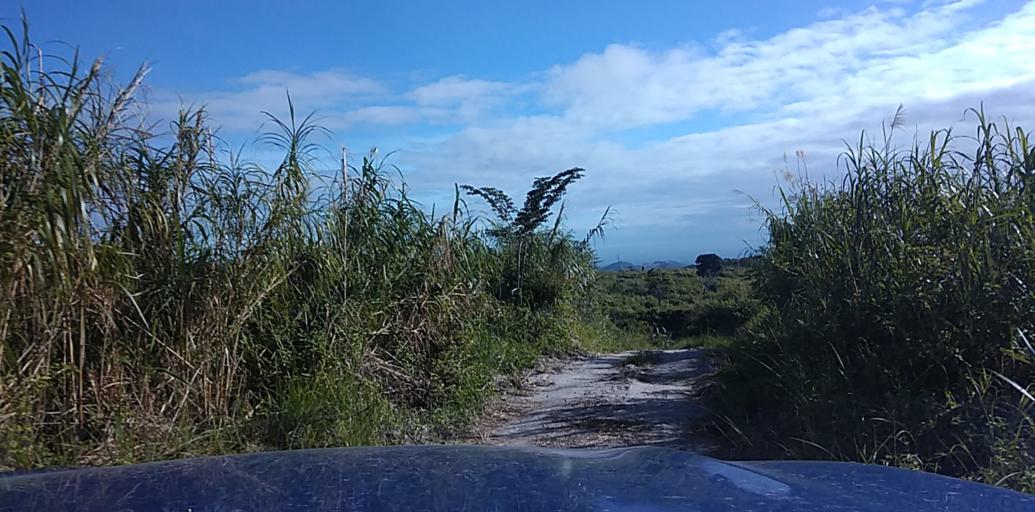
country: PH
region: Central Luzon
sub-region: Province of Pampanga
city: Babo-Pangulo
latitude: 15.1505
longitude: 120.4314
